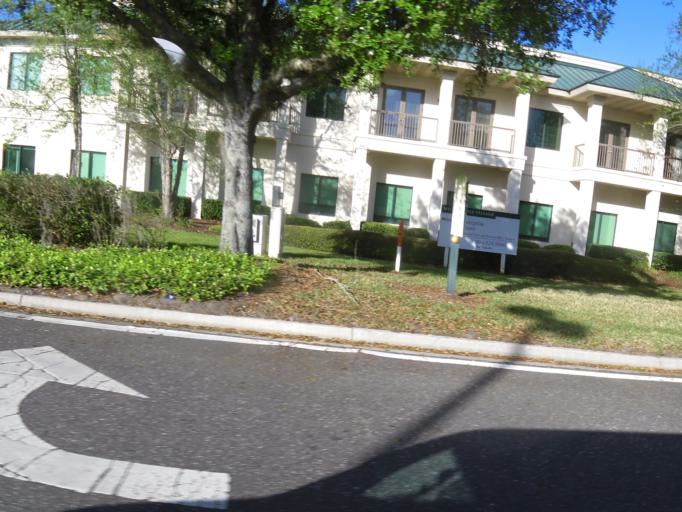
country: US
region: Florida
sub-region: Saint Johns County
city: Villano Beach
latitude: 29.9851
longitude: -81.4681
